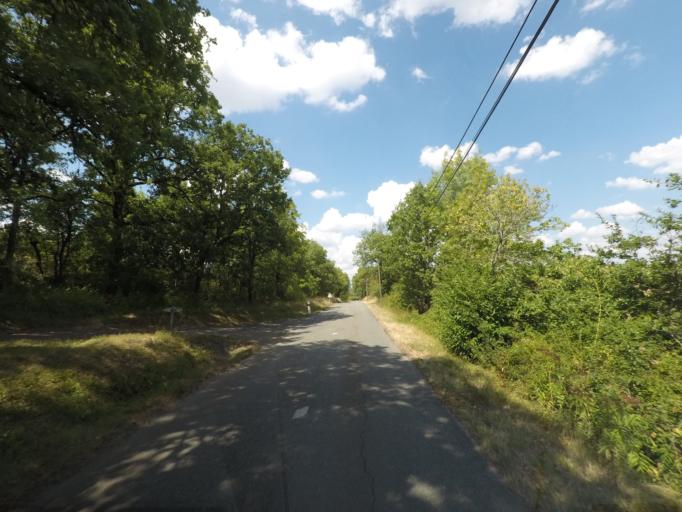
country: FR
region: Midi-Pyrenees
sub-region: Departement du Lot
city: Cahors
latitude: 44.5823
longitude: 1.5777
